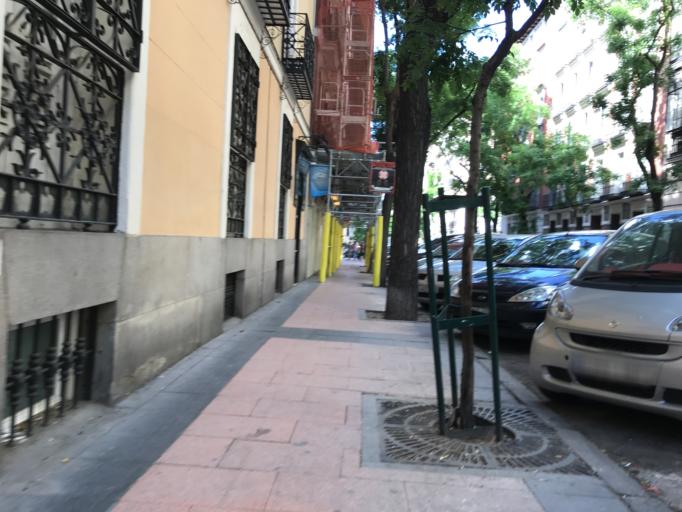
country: ES
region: Madrid
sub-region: Provincia de Madrid
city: Retiro
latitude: 40.4217
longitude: -3.6858
